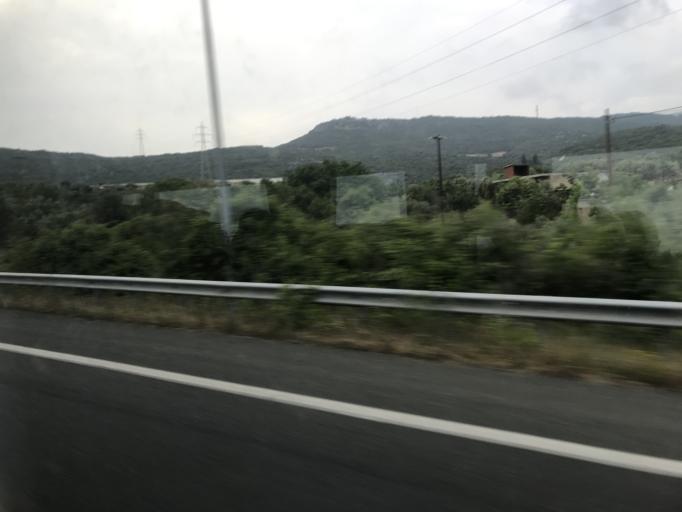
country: GR
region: East Macedonia and Thrace
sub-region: Nomos Evrou
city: Alexandroupoli
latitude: 40.8600
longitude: 25.7469
